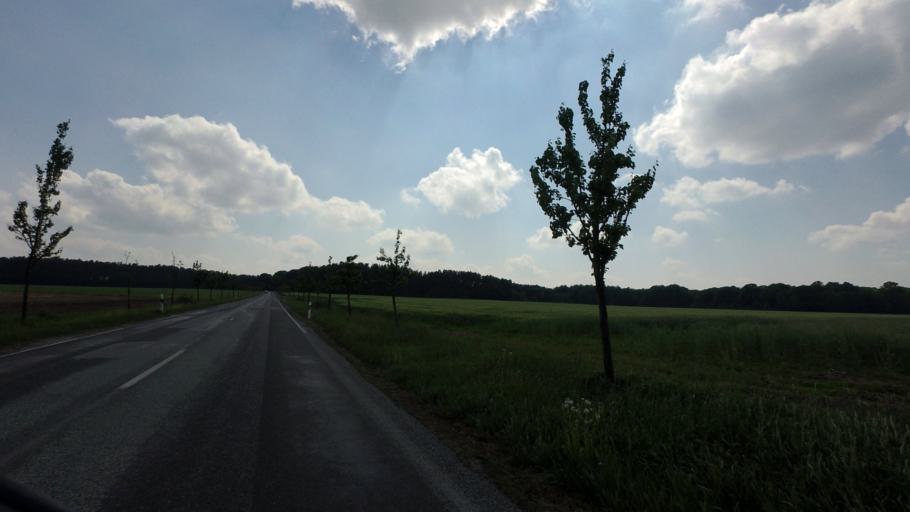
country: DE
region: Saxony
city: Mucka
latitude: 51.2907
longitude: 14.6599
